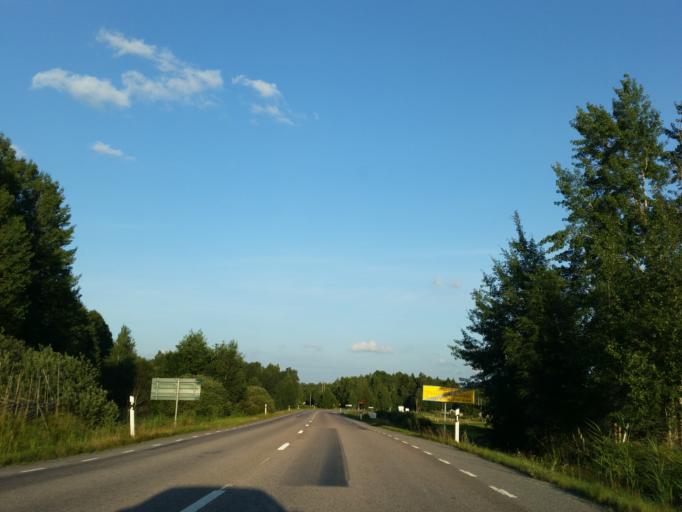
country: SE
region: Stockholm
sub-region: Sodertalje Kommun
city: Soedertaelje
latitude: 59.2215
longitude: 17.5686
